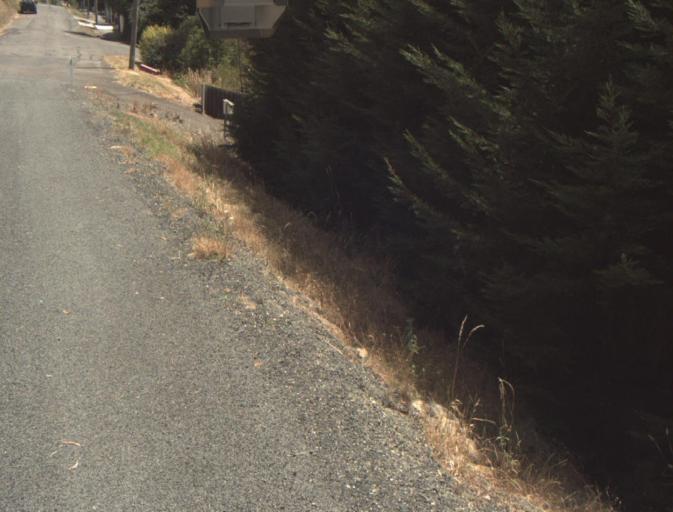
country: AU
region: Tasmania
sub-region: Launceston
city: West Launceston
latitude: -41.4545
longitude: 147.1321
